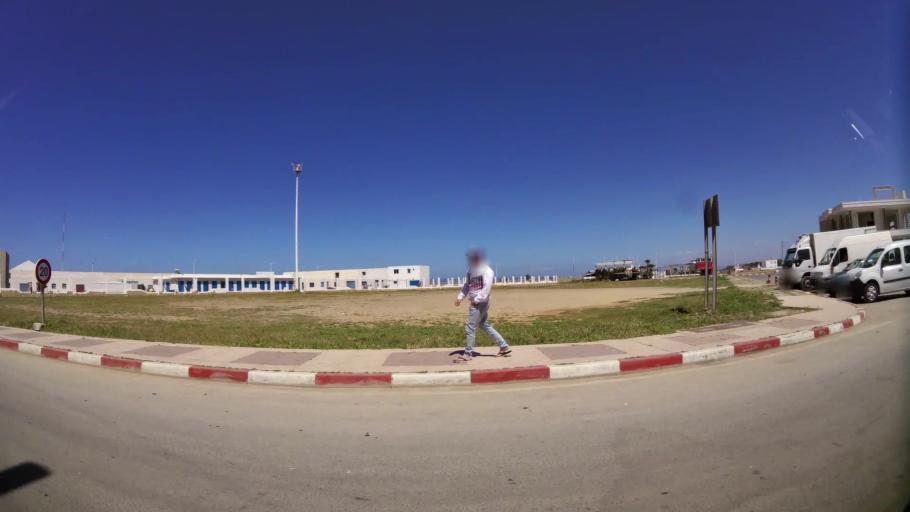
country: MA
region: Oriental
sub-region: Berkane-Taourirt
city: Madagh
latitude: 35.1429
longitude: -2.4240
